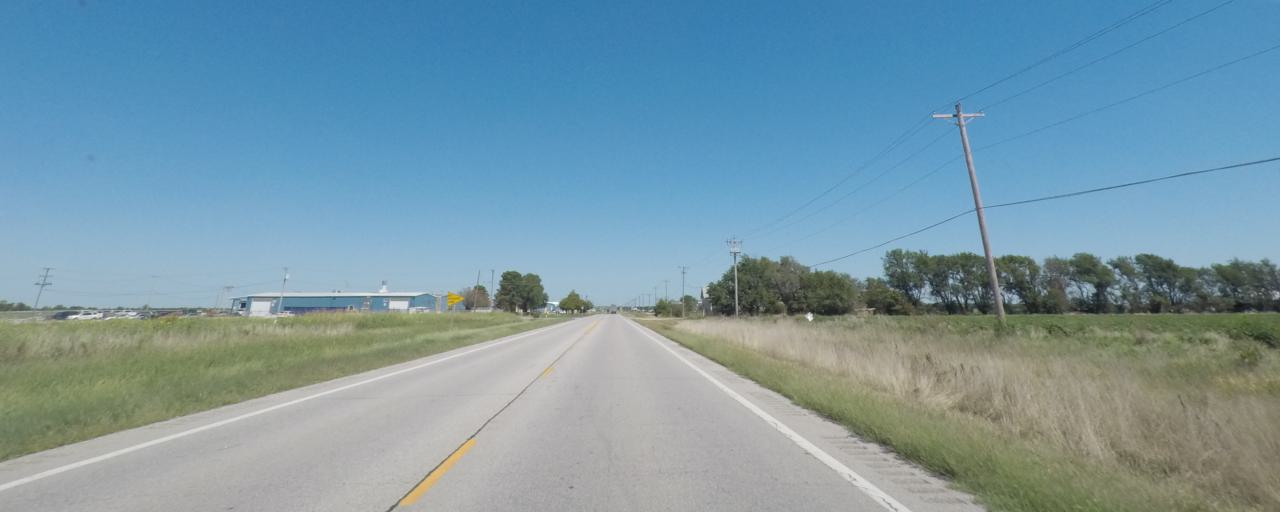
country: US
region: Kansas
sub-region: Sumner County
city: Wellington
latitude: 37.3173
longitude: -97.3847
